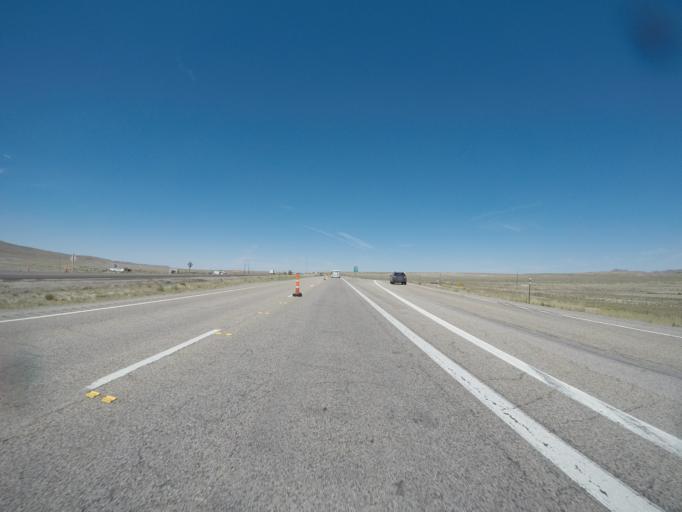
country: US
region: Wyoming
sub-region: Carbon County
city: Rawlins
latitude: 41.7537
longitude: -106.9580
